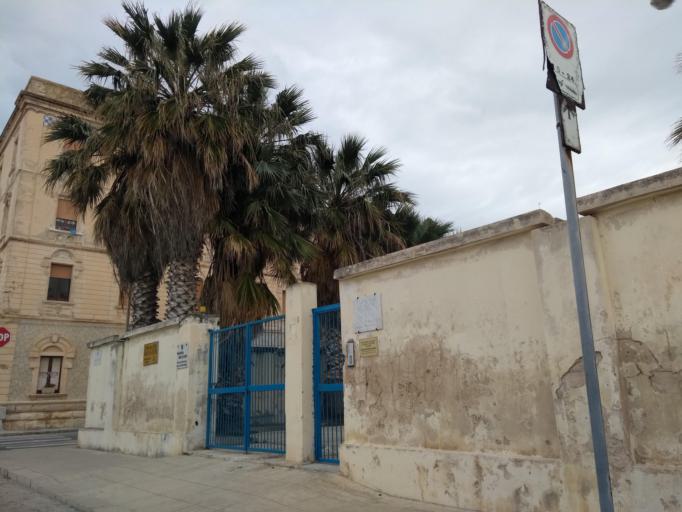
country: IT
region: Sicily
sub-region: Trapani
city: Trapani
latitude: 38.0160
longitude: 12.5012
